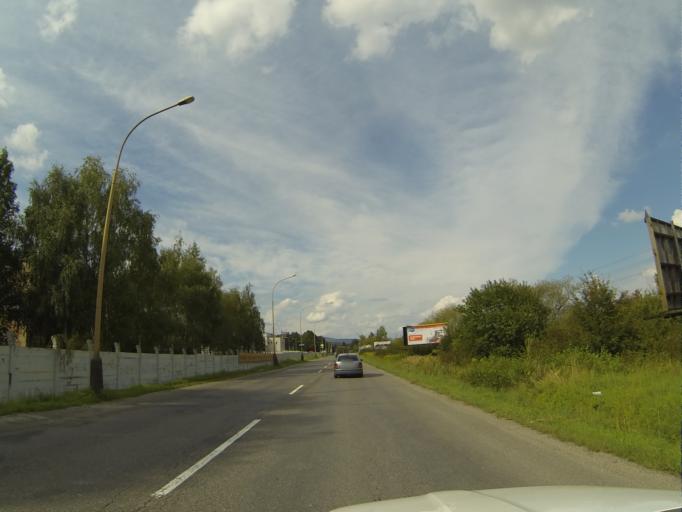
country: SK
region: Nitriansky
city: Novaky
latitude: 48.7057
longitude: 18.5367
